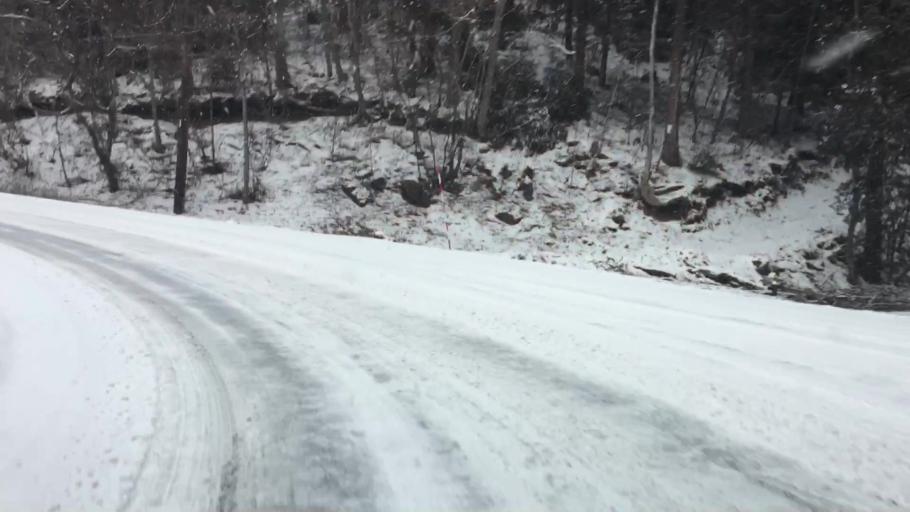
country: JP
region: Tochigi
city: Imaichi
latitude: 36.8789
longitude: 139.7311
